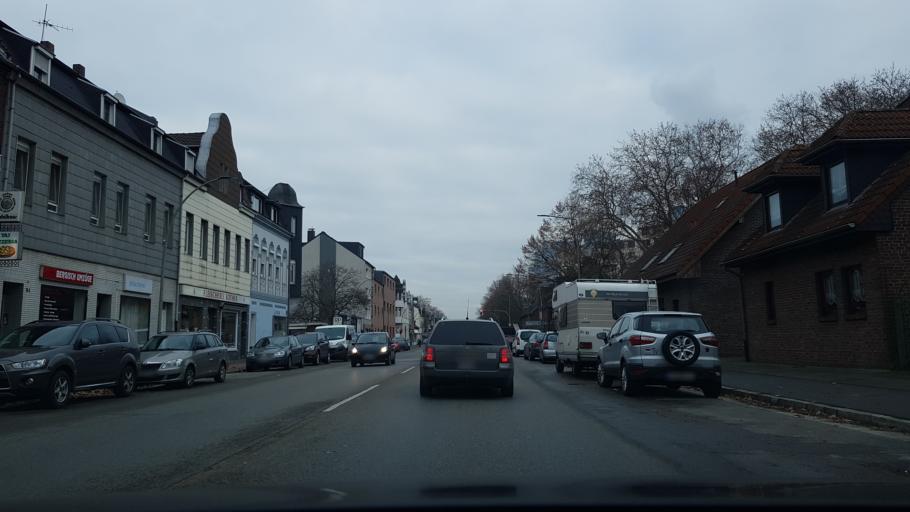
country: DE
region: North Rhine-Westphalia
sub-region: Regierungsbezirk Dusseldorf
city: Moers
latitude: 51.4463
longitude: 6.6884
